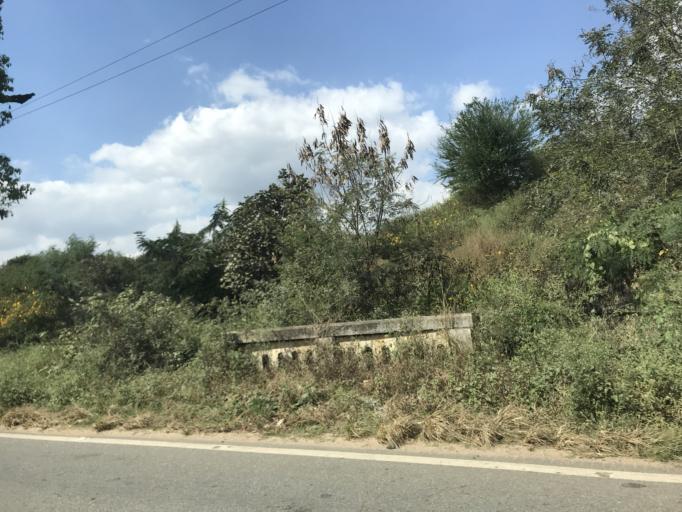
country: IN
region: Karnataka
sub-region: Hassan
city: Hassan
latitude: 12.9934
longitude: 76.0671
